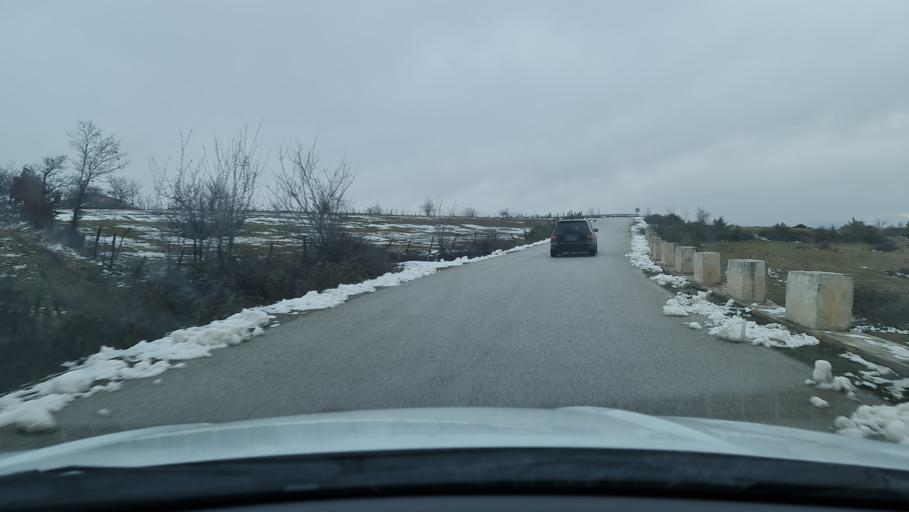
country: AL
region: Kukes
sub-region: Rrethi i Kukesit
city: Kolsh
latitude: 42.0705
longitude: 20.3249
